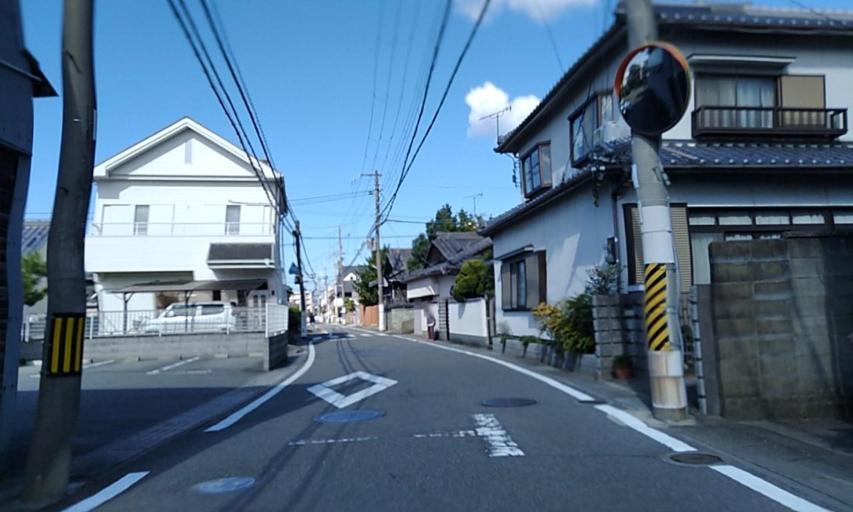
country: JP
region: Wakayama
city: Kainan
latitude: 34.1905
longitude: 135.1895
